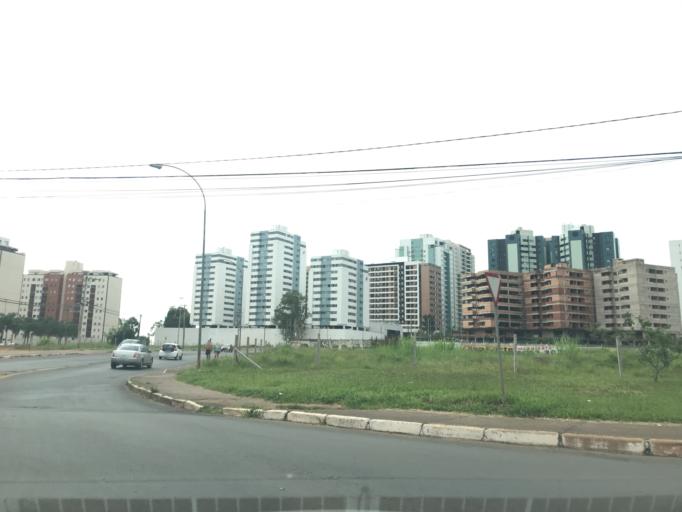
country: BR
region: Federal District
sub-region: Brasilia
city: Brasilia
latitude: -15.8318
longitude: -48.0123
